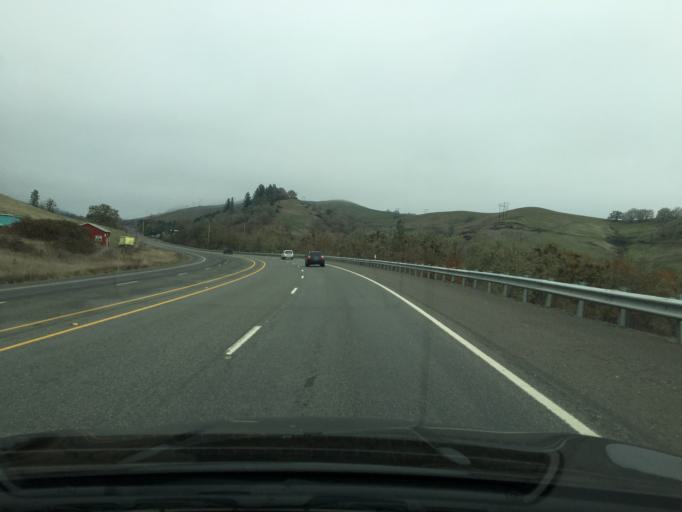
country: US
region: Oregon
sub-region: Douglas County
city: Roseburg North
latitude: 43.2120
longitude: -123.2438
